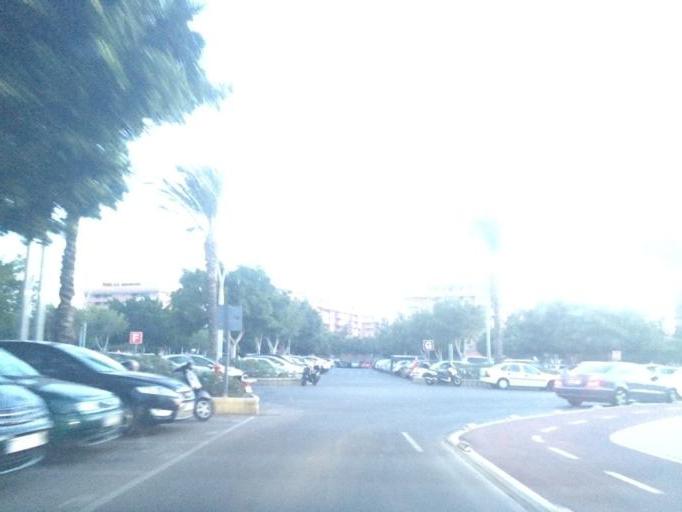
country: ES
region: Andalusia
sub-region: Provincia de Almeria
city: Almeria
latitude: 36.8394
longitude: -2.4337
